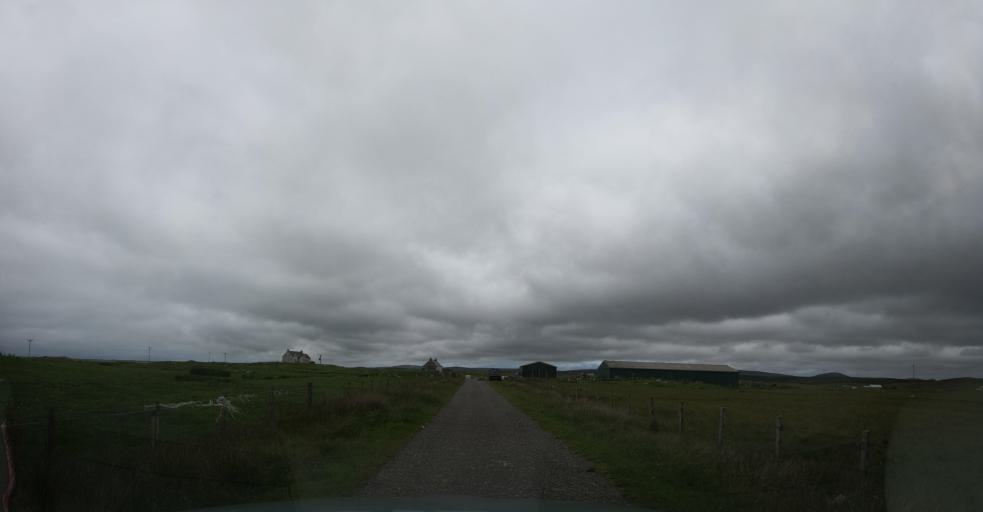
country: GB
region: Scotland
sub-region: Eilean Siar
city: Isle of North Uist
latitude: 57.5474
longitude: -7.3454
